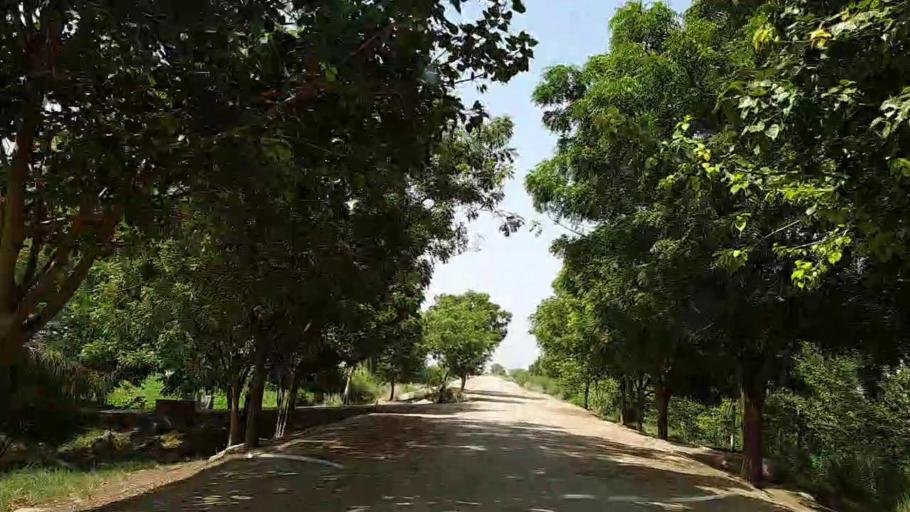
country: PK
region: Sindh
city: Kandiaro
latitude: 27.0478
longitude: 68.1332
